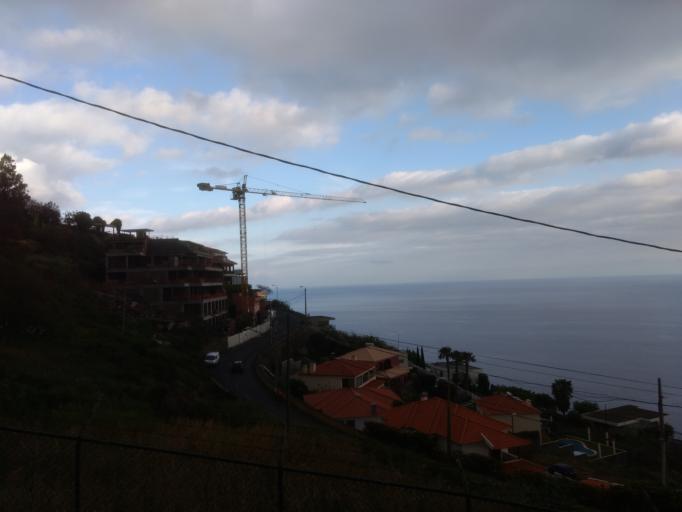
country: PT
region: Madeira
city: Canico
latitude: 32.6476
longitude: -16.8740
